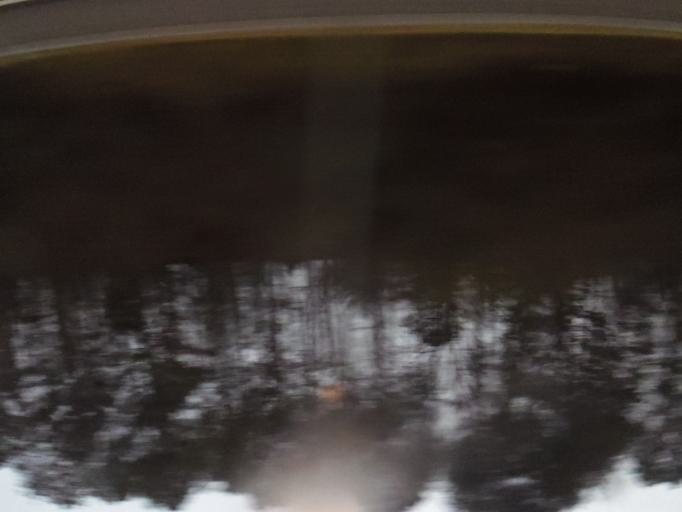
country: US
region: Alabama
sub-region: Cullman County
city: Cullman
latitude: 34.2037
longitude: -86.8783
